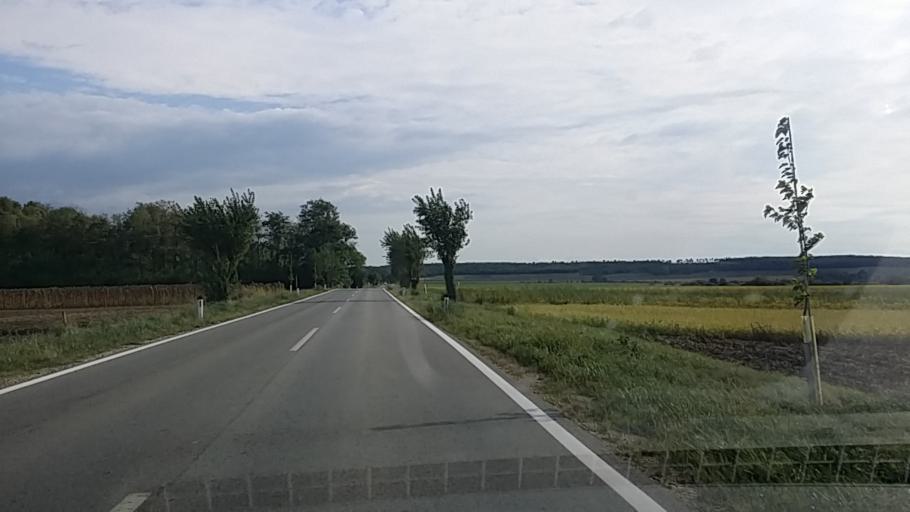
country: AT
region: Burgenland
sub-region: Eisenstadt-Umgebung
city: Sankt Margarethen im Burgenland
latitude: 47.7903
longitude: 16.6179
